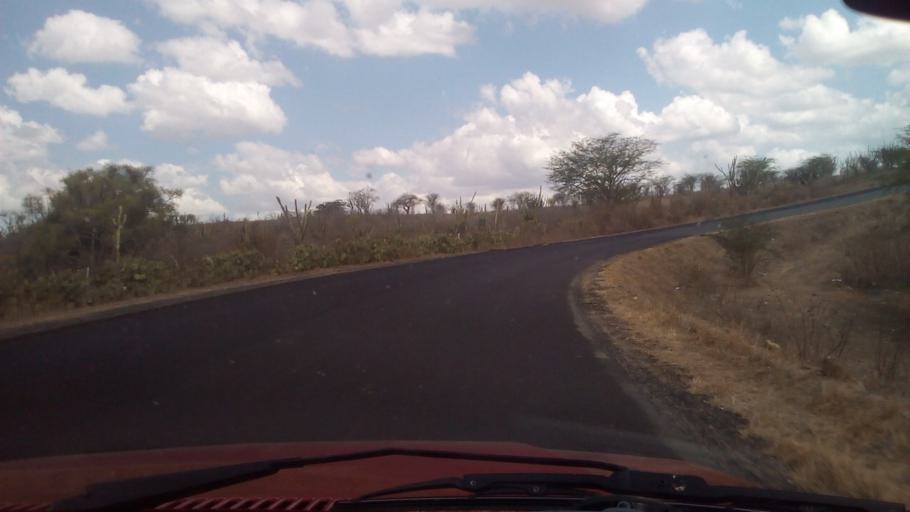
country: BR
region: Paraiba
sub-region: Bananeiras
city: Bananeiras
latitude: -6.7148
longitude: -35.7199
